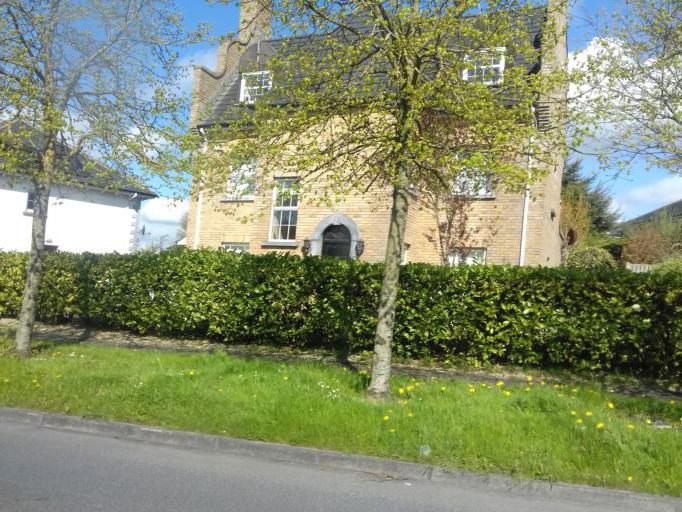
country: IE
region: Leinster
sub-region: Laois
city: Portlaoise
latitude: 53.0430
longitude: -7.2654
